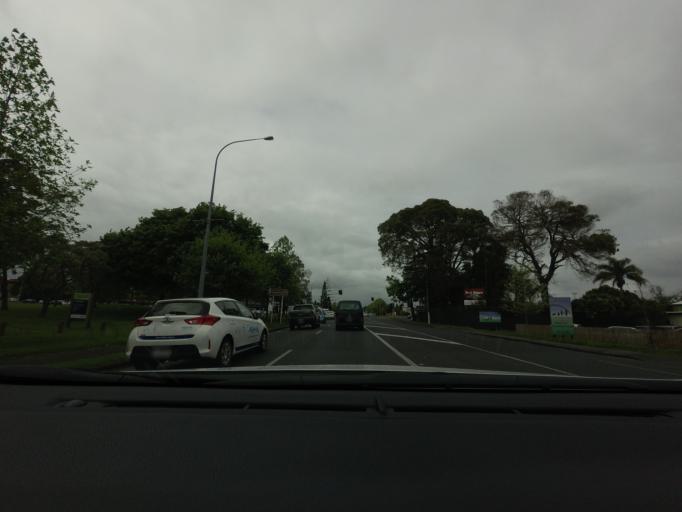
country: NZ
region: Auckland
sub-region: Auckland
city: Rosebank
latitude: -36.8613
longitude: 174.6295
